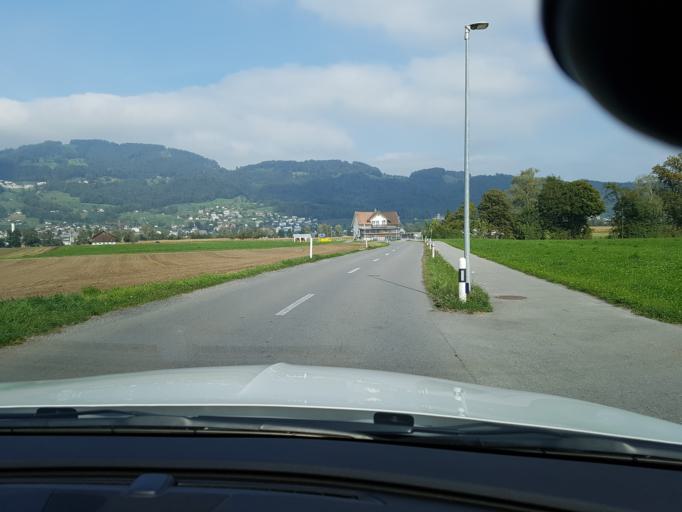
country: CH
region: Saint Gallen
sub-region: Wahlkreis Rheintal
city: Rebstein
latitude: 47.3871
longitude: 9.5965
